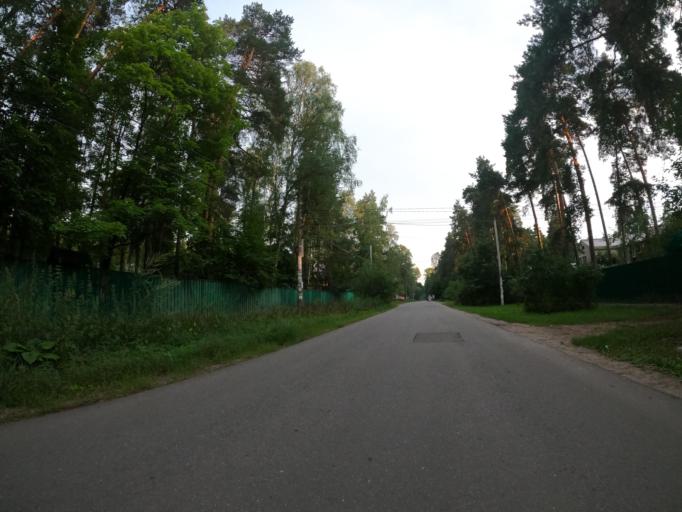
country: RU
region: Moskovskaya
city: Bykovo
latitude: 55.6354
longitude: 38.0796
